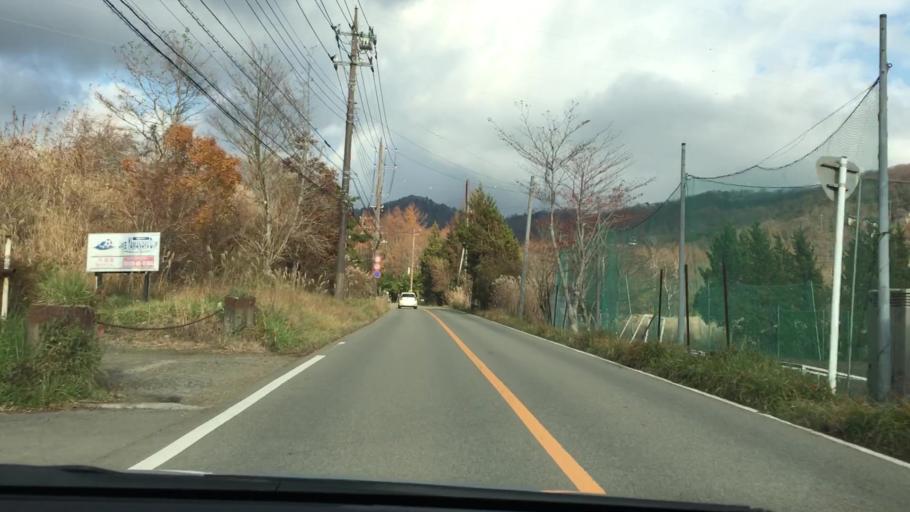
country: JP
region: Shizuoka
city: Gotemba
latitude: 35.4384
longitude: 138.9184
